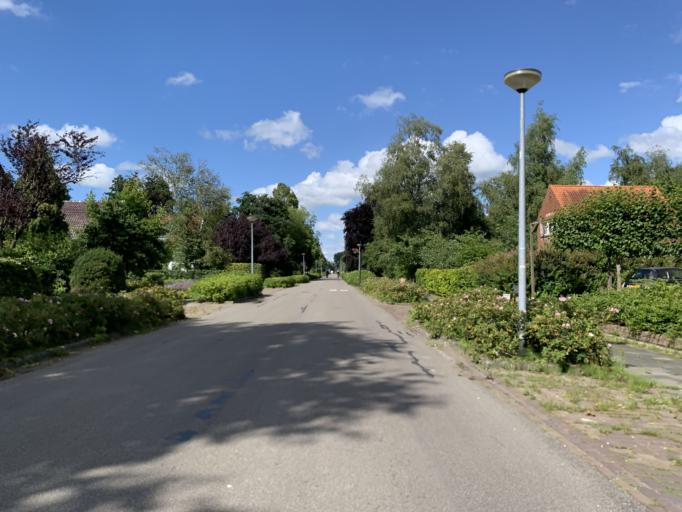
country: NL
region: Groningen
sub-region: Gemeente Groningen
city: Groningen
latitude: 53.1839
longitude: 6.5500
